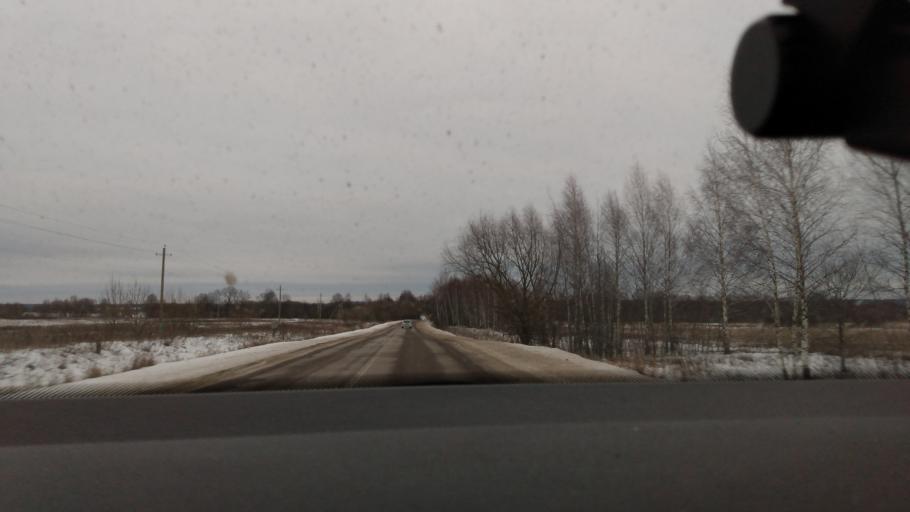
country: RU
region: Moskovskaya
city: Krasnaya Poyma
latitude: 55.1674
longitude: 39.1710
